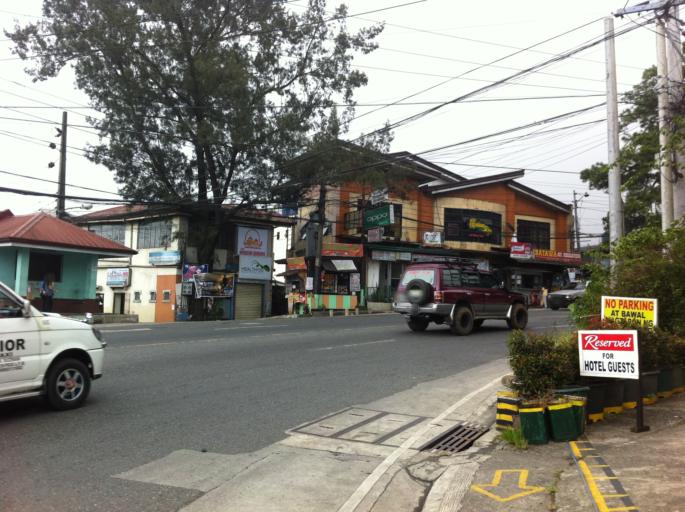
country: PH
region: Cordillera
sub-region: Baguio City
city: Baguio
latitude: 16.4236
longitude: 120.5933
